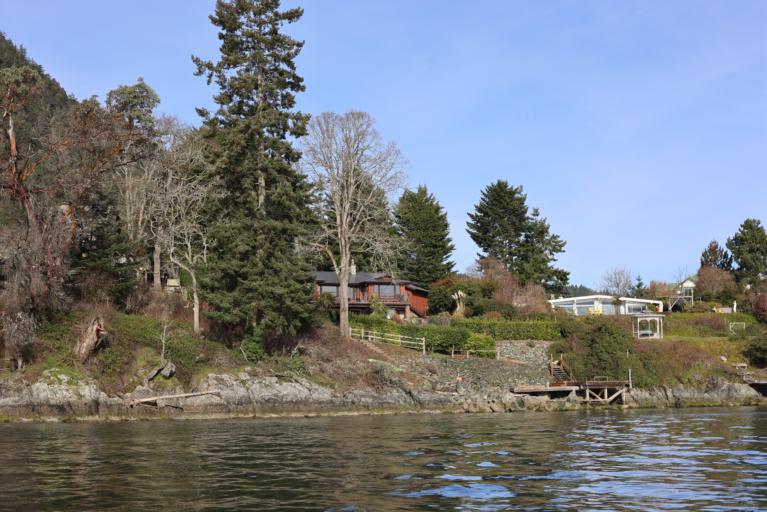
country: CA
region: British Columbia
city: Duncan
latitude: 48.7568
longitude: -123.5975
